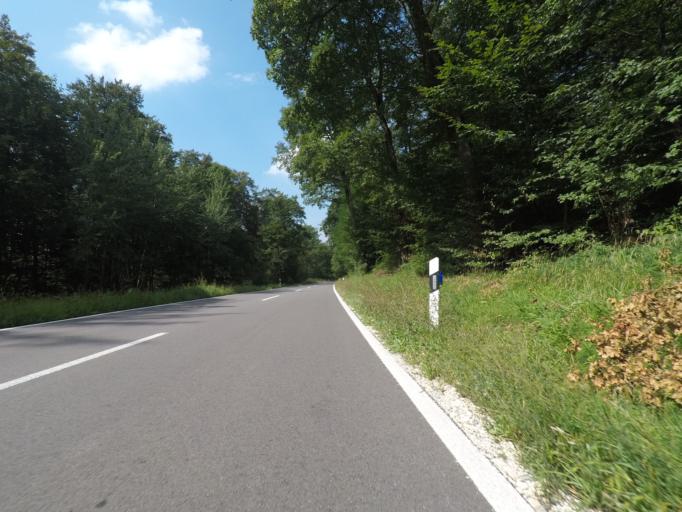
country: DE
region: Baden-Wuerttemberg
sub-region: Regierungsbezirk Stuttgart
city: Winterbach
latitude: 48.7857
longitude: 9.4414
